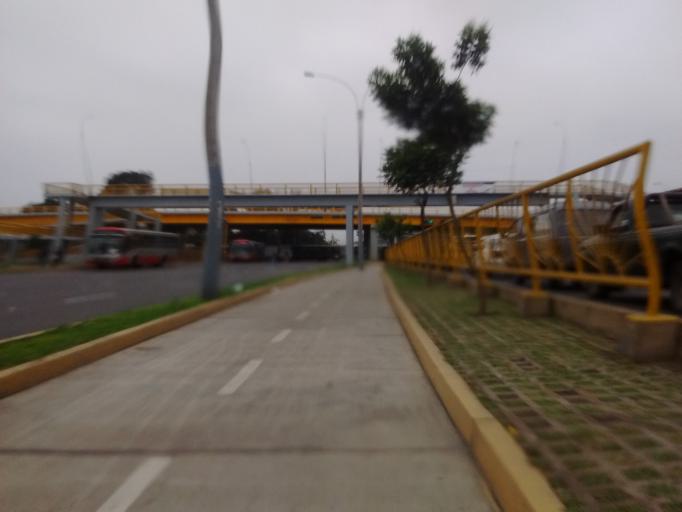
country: PE
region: Callao
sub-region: Callao
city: Callao
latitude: -12.0611
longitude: -77.0789
